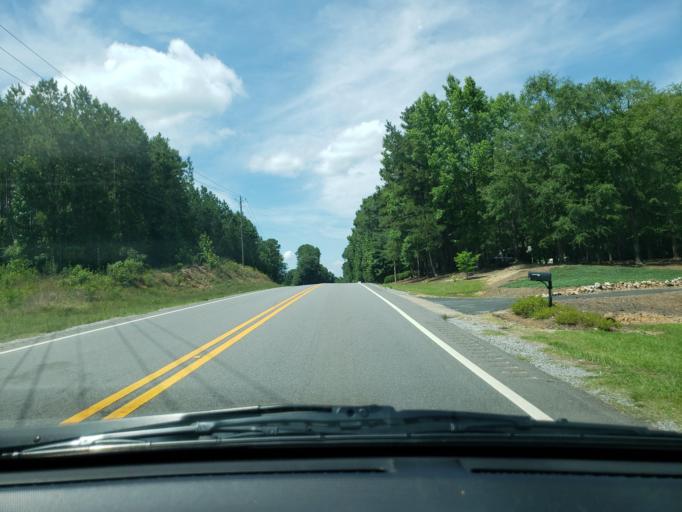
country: US
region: Alabama
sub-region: Elmore County
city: Eclectic
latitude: 32.6349
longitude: -85.9541
